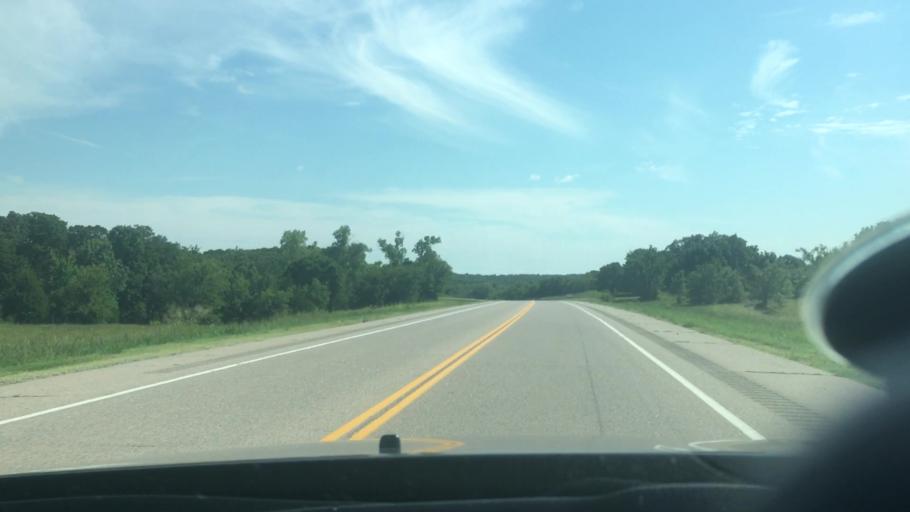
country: US
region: Oklahoma
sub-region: Seminole County
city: Seminole
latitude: 35.1376
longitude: -96.6776
